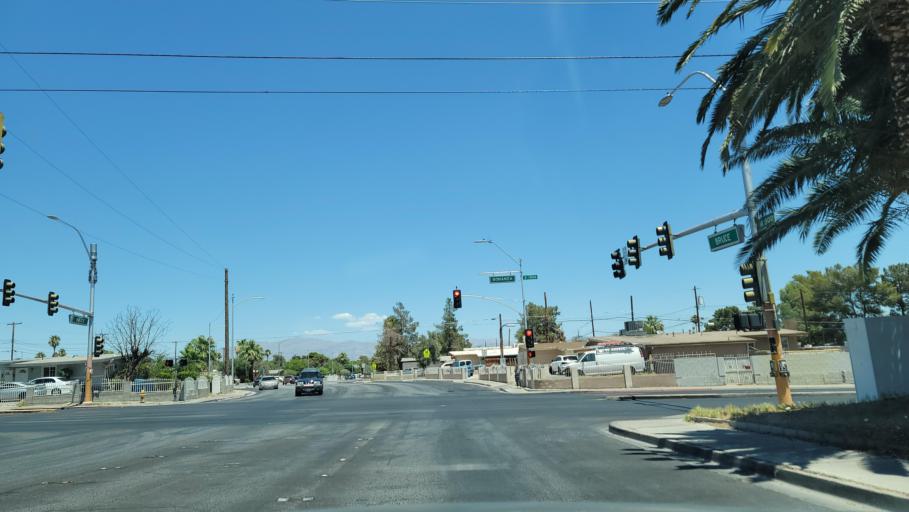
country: US
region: Nevada
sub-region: Clark County
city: Las Vegas
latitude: 36.1737
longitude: -115.1251
